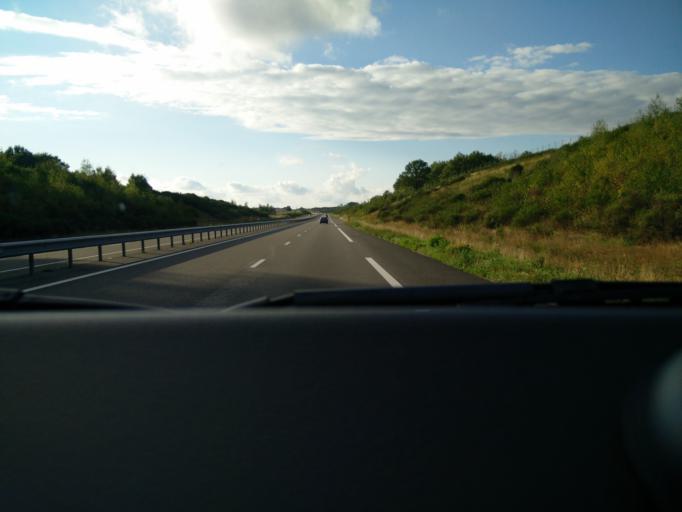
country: FR
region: Lorraine
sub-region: Departement de Meurthe-et-Moselle
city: Baccarat
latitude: 48.5189
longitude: 6.6472
